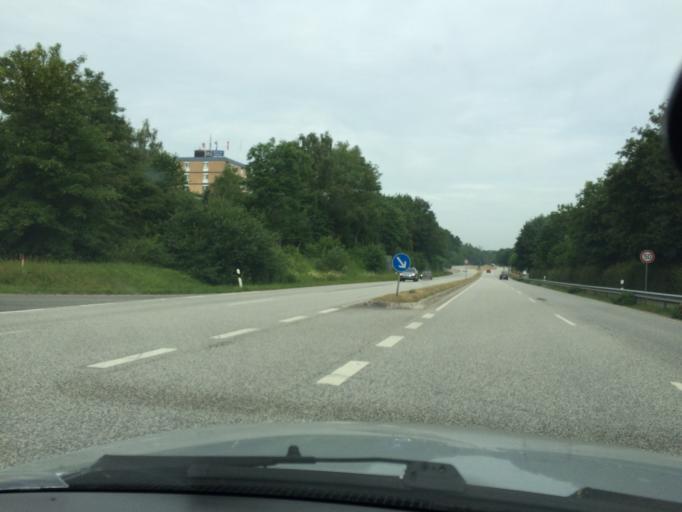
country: DK
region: South Denmark
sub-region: Aabenraa Kommune
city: Krusa
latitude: 54.8361
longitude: 9.4106
